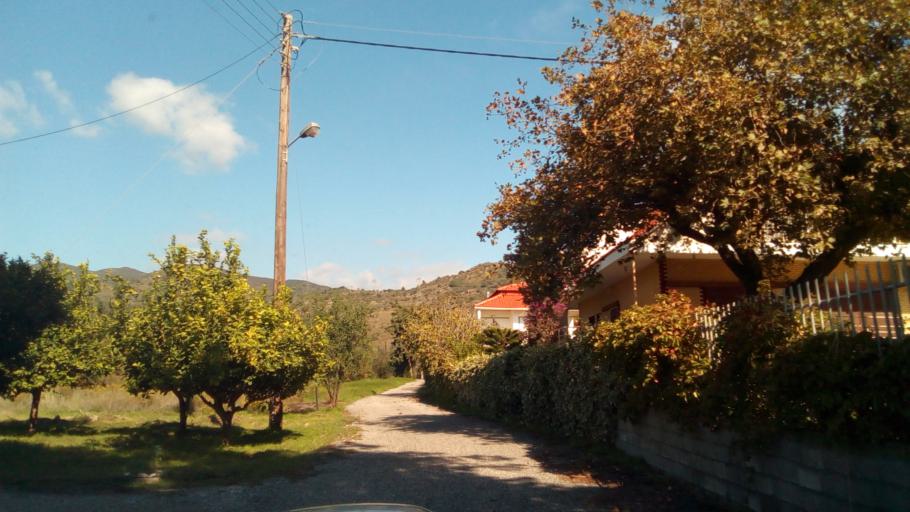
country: GR
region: West Greece
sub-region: Nomos Aitolias kai Akarnanias
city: Antirrio
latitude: 38.3469
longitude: 21.7167
